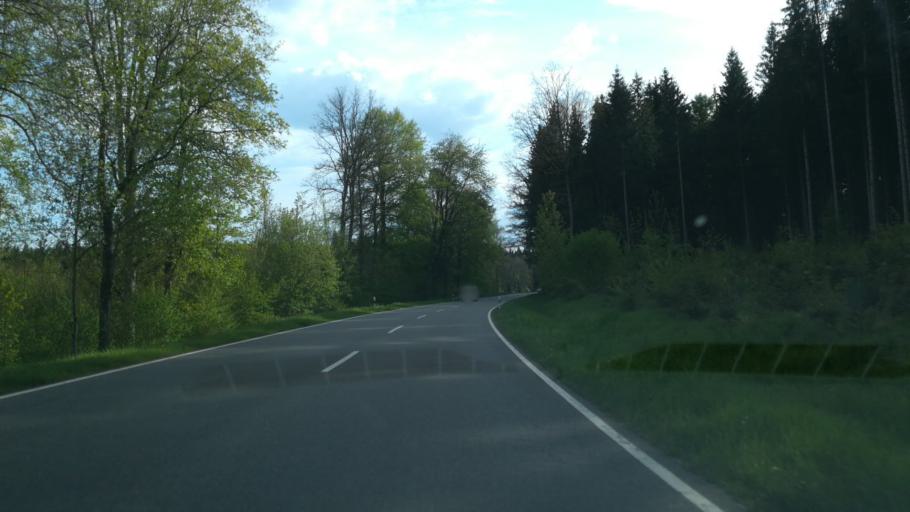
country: DE
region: Baden-Wuerttemberg
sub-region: Tuebingen Region
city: Messkirch
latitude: 47.9730
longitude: 9.0778
